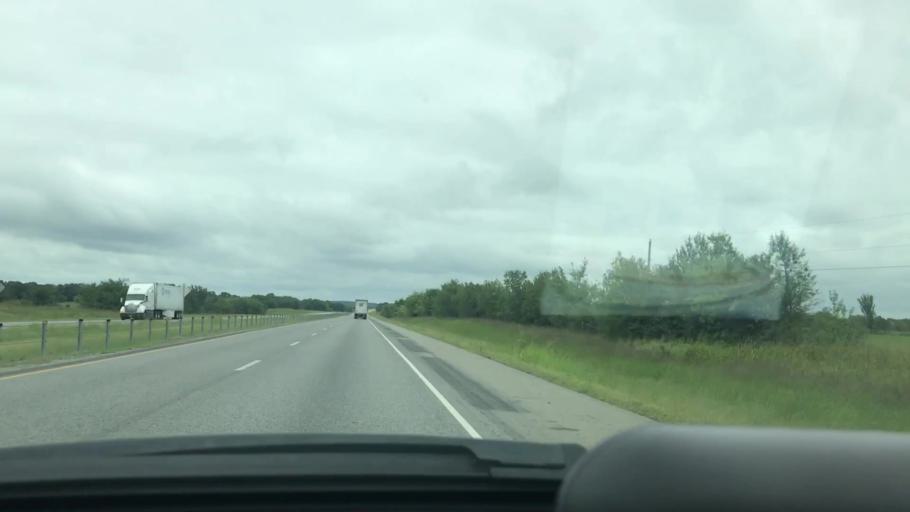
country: US
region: Oklahoma
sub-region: Pittsburg County
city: McAlester
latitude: 34.7544
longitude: -95.8927
